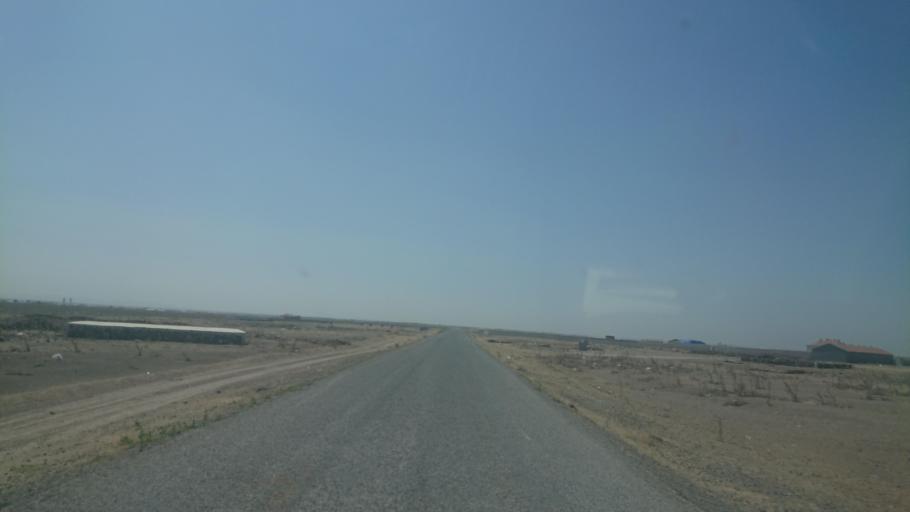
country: TR
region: Aksaray
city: Yesilova
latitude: 38.3293
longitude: 33.7487
